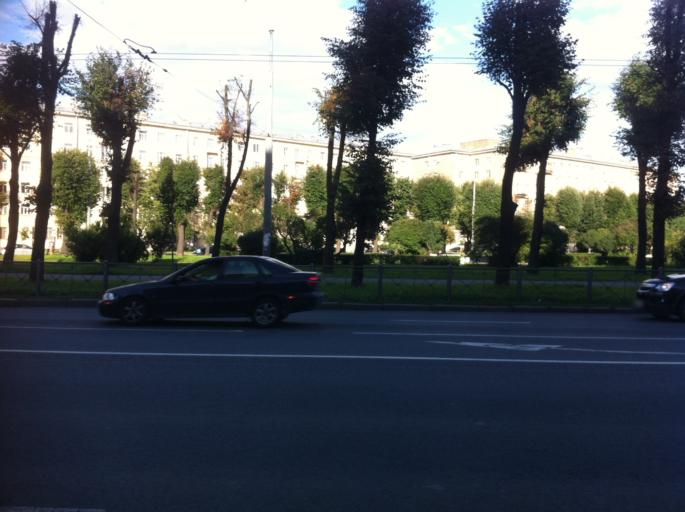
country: RU
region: St.-Petersburg
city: Avtovo
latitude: 59.8749
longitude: 30.2583
